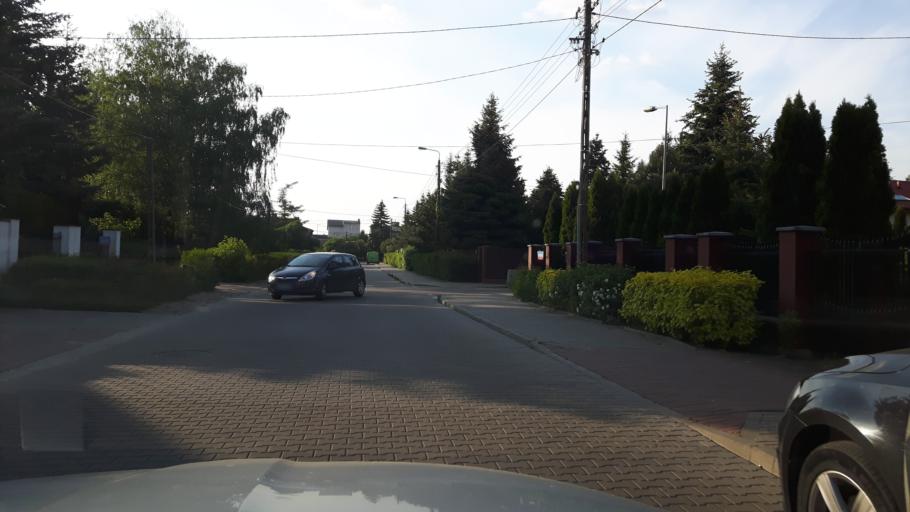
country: PL
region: Masovian Voivodeship
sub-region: Warszawa
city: Rembertow
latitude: 52.2638
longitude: 21.1621
